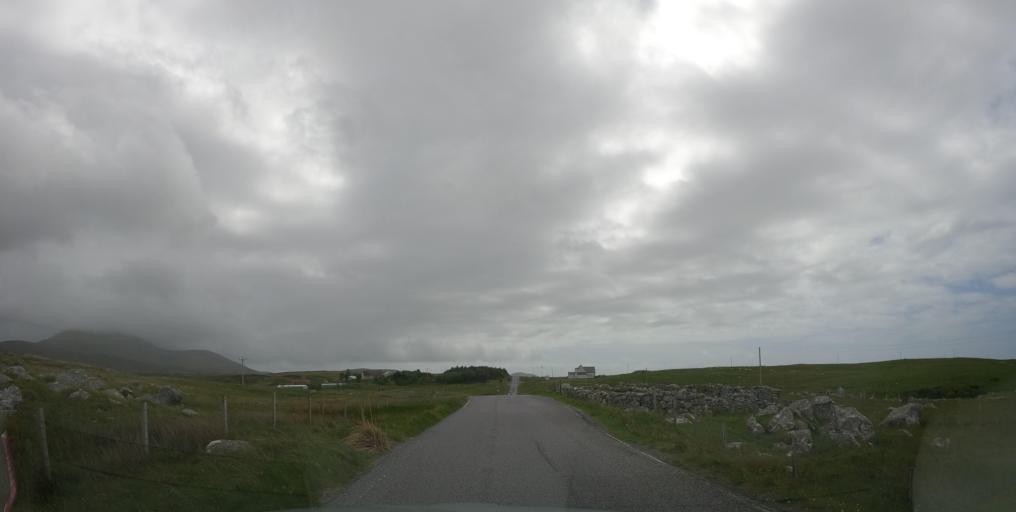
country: GB
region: Scotland
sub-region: Eilean Siar
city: Isle of South Uist
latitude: 57.2890
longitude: -7.3664
